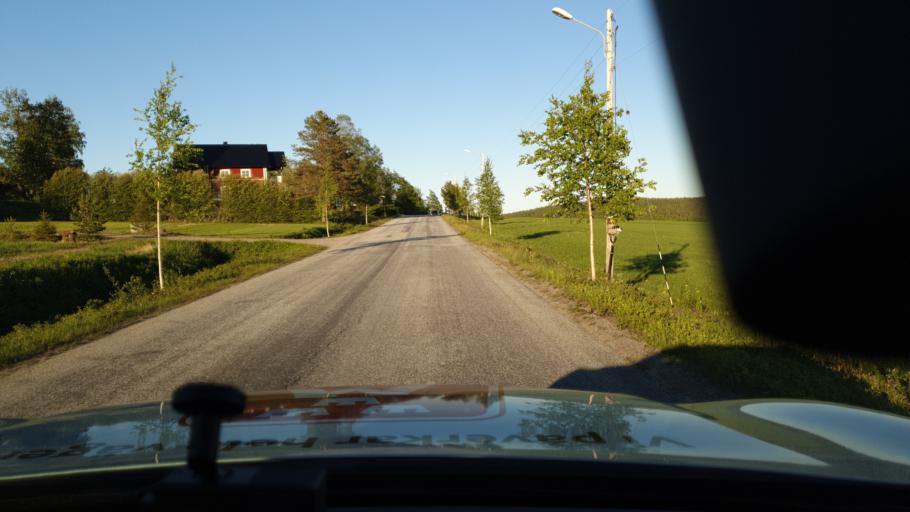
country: SE
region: Vaesterbotten
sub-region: Umea Kommun
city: Roback
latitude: 64.0136
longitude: 20.1349
